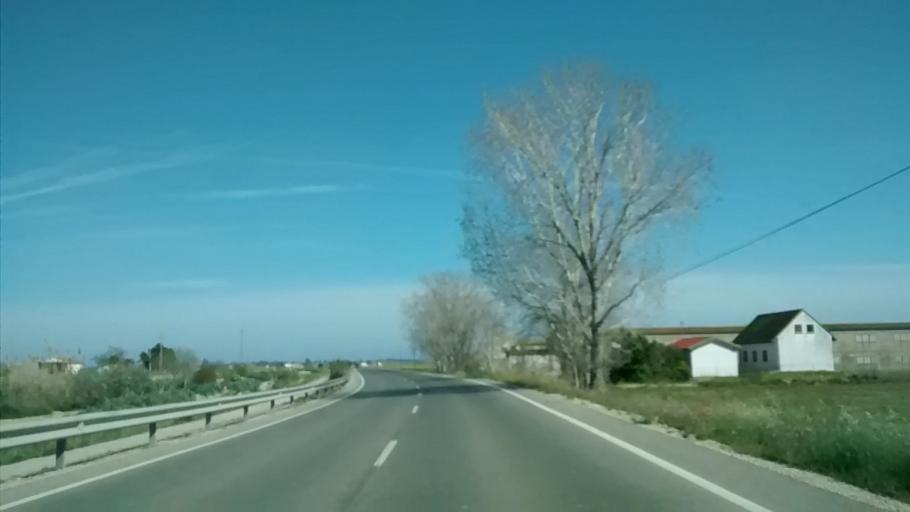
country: ES
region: Catalonia
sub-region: Provincia de Tarragona
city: Deltebre
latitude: 40.7048
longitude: 0.7868
